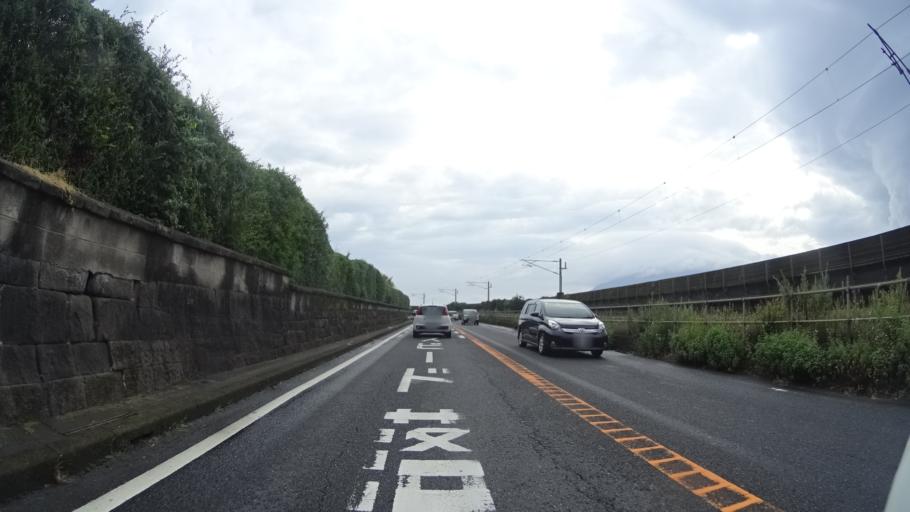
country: JP
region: Kagoshima
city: Kagoshima-shi
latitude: 31.6180
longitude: 130.5803
